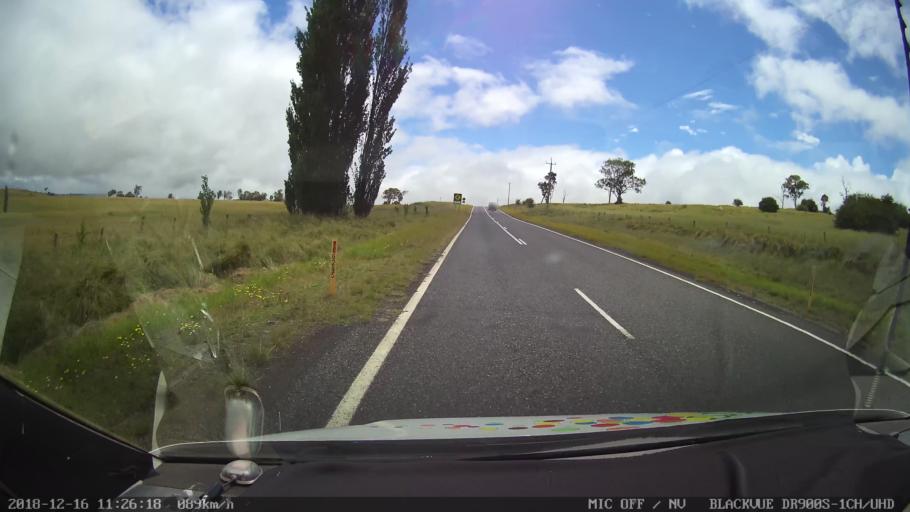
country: AU
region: New South Wales
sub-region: Tenterfield Municipality
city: Carrolls Creek
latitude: -29.0521
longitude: 152.0728
